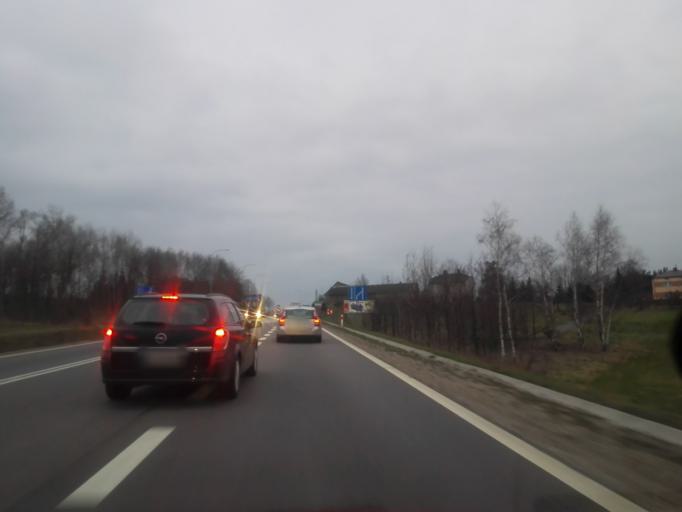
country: PL
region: Podlasie
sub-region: Powiat lomzynski
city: Piatnica
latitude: 53.2316
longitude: 22.1125
